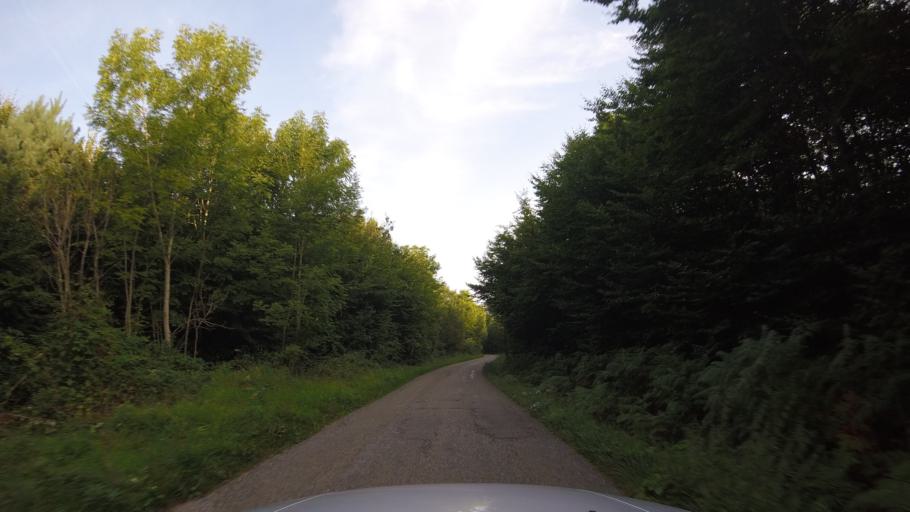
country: DE
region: Baden-Wuerttemberg
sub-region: Regierungsbezirk Stuttgart
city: Aspach
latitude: 49.0027
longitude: 9.3876
